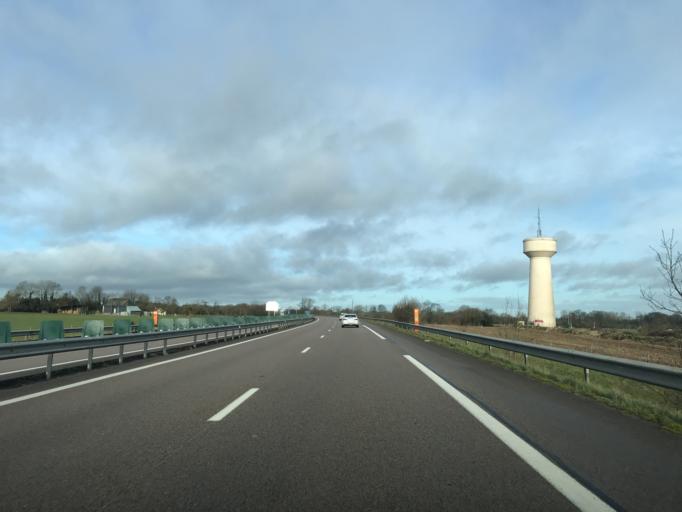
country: FR
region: Haute-Normandie
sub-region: Departement de l'Eure
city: Beuzeville
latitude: 49.3352
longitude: 0.3841
